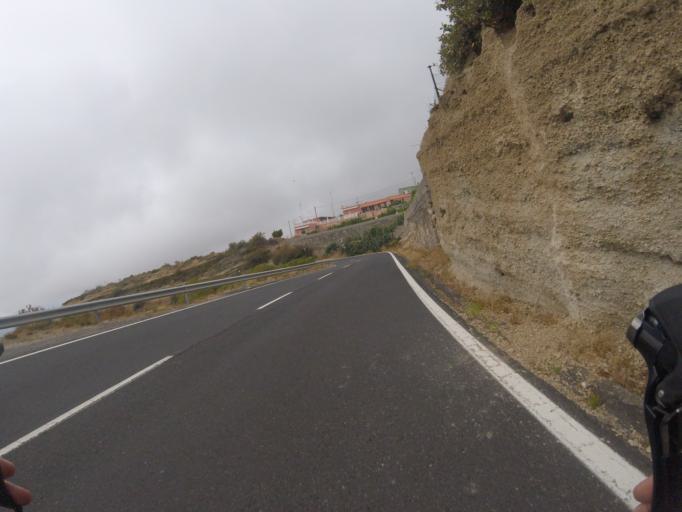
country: ES
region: Canary Islands
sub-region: Provincia de Santa Cruz de Tenerife
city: Fasnia
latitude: 28.2223
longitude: -16.4492
